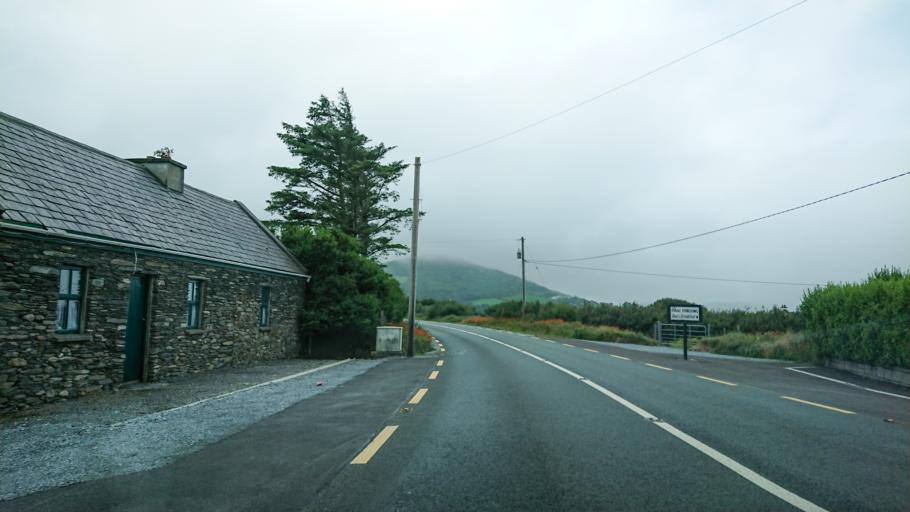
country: IE
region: Munster
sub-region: Ciarrai
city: Cahersiveen
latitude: 51.9552
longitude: -10.1947
